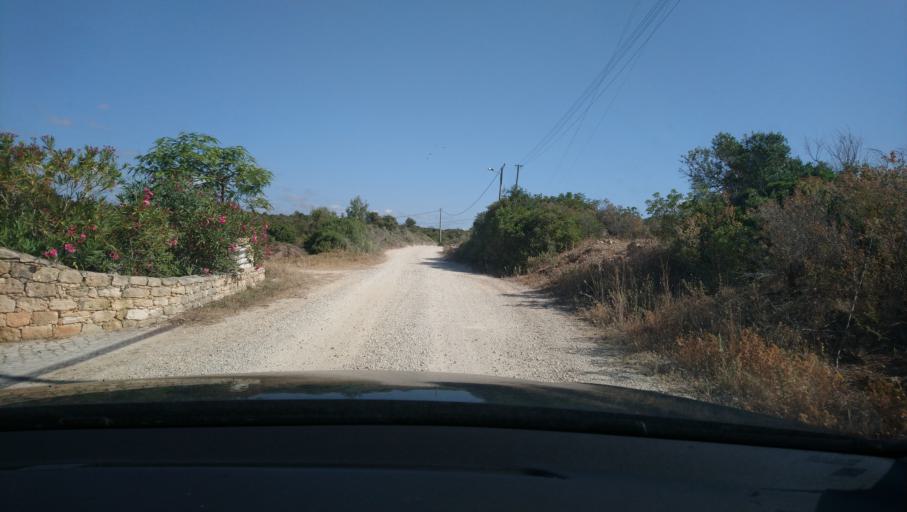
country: PT
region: Faro
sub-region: Silves
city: Armacao de Pera
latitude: 37.0939
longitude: -8.3992
